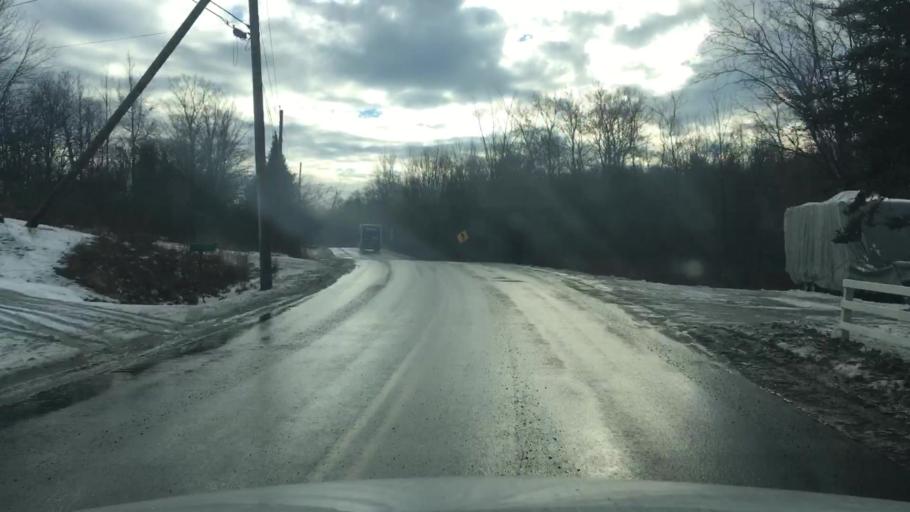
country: US
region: Maine
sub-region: Penobscot County
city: Brewer
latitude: 44.7621
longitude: -68.7754
